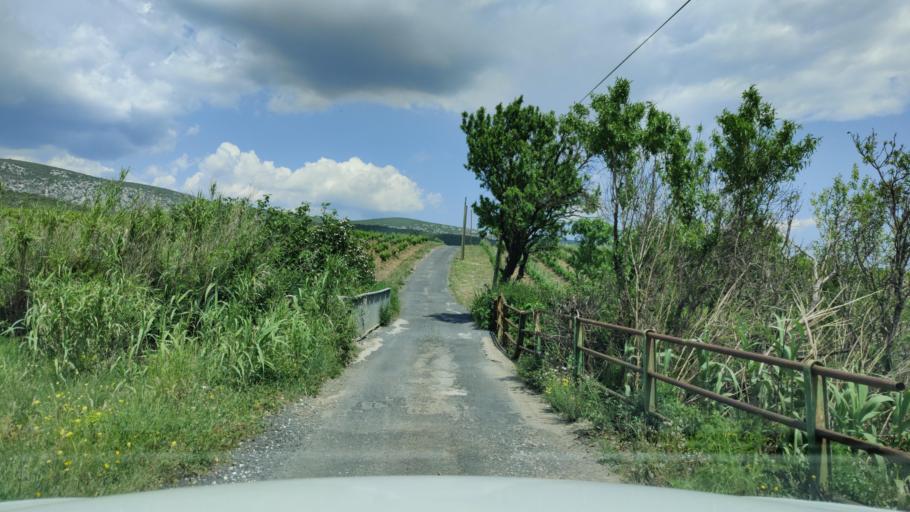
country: FR
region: Languedoc-Roussillon
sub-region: Departement des Pyrenees-Orientales
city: Estagel
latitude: 42.8127
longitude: 2.6697
